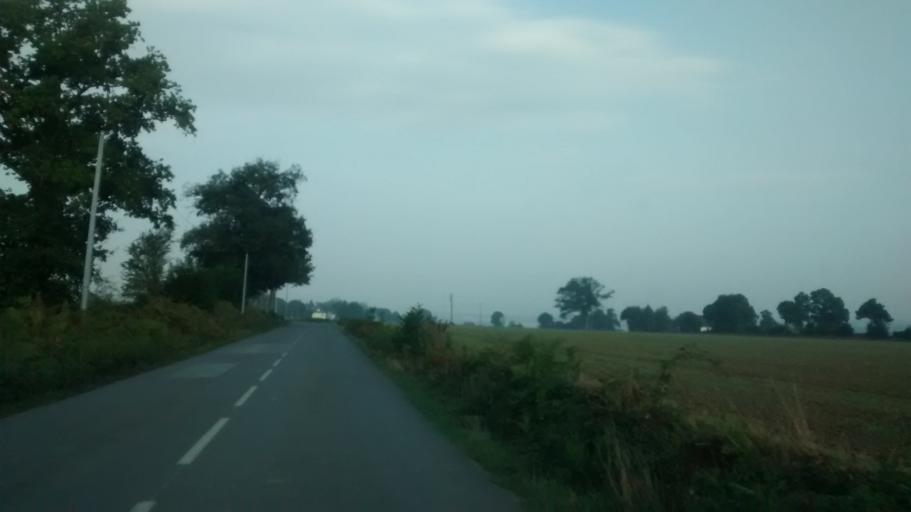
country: FR
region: Brittany
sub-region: Departement d'Ille-et-Vilaine
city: Poce-les-Bois
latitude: 48.1342
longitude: -1.2506
